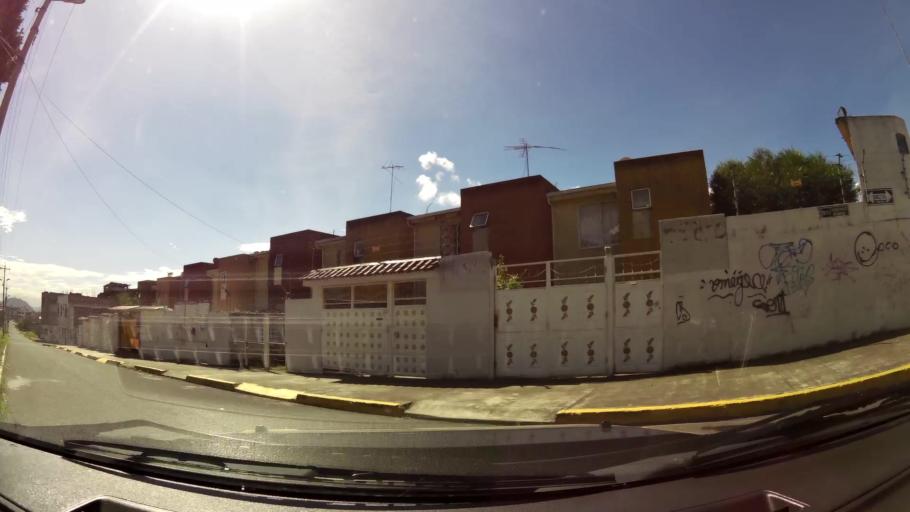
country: EC
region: Pichincha
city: Quito
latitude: -0.2878
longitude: -78.5593
